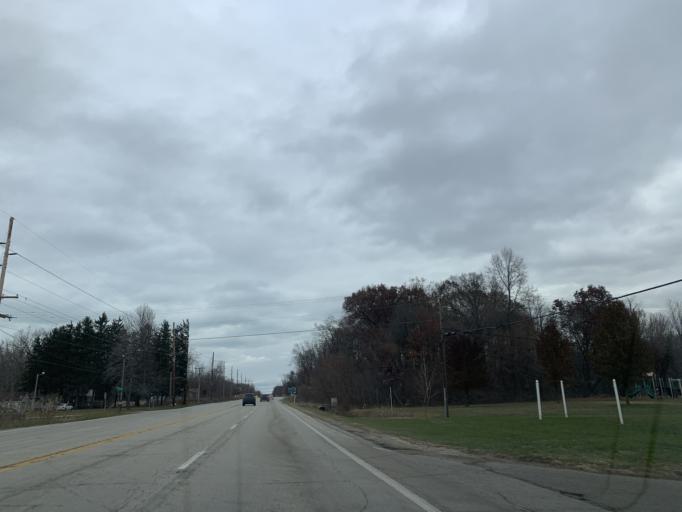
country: US
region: Indiana
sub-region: LaPorte County
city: Long Beach
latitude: 41.7178
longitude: -86.8260
